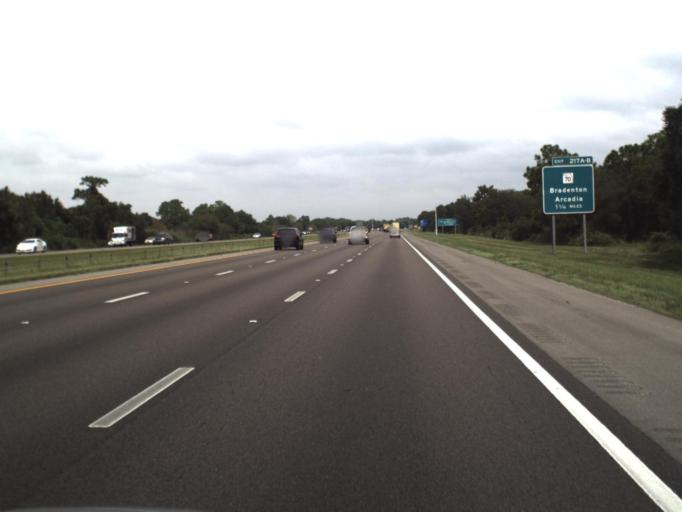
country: US
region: Florida
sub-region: Sarasota County
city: Desoto Lakes
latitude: 27.4188
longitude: -82.4569
